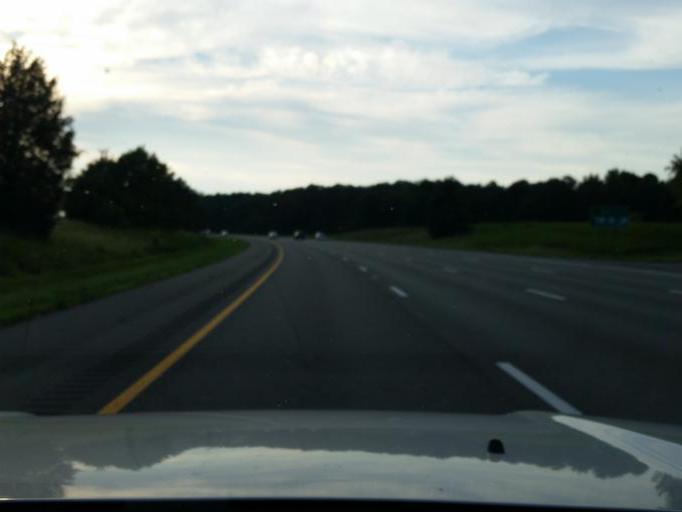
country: US
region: Virginia
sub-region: Hanover County
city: Mechanicsville
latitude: 37.6297
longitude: -77.3721
